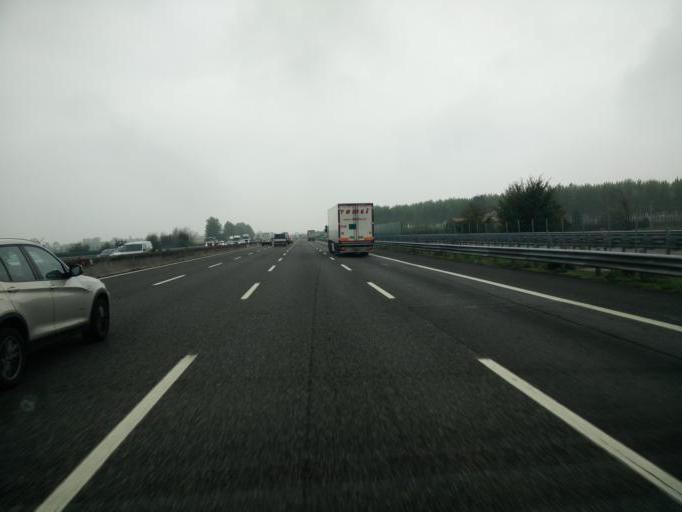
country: IT
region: Emilia-Romagna
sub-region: Provincia di Modena
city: Baggiovara
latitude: 44.6106
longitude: 10.9036
